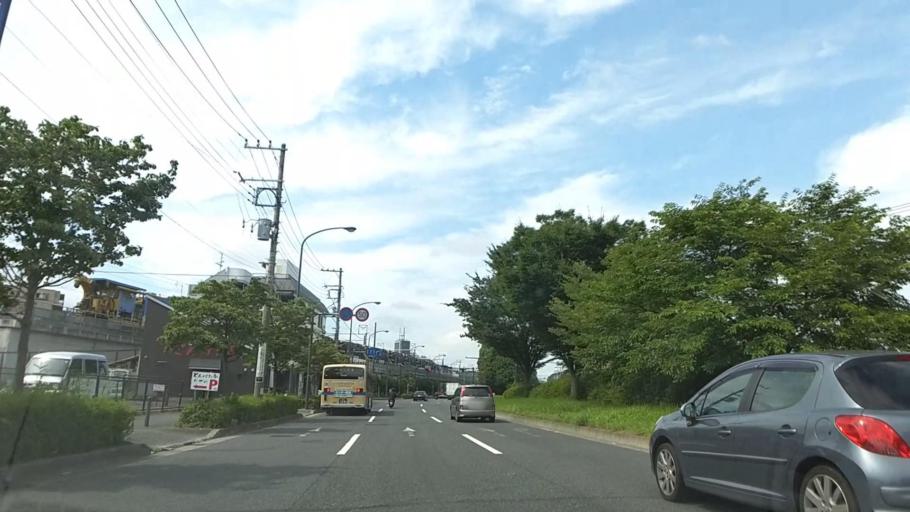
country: JP
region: Kanagawa
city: Yokohama
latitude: 35.4995
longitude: 139.6070
